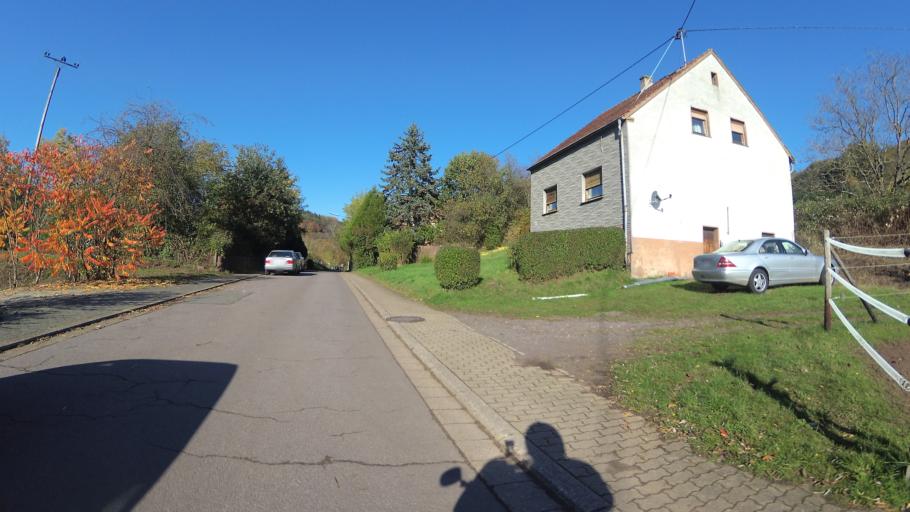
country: DE
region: Saarland
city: Losheim
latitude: 49.4633
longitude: 6.7559
